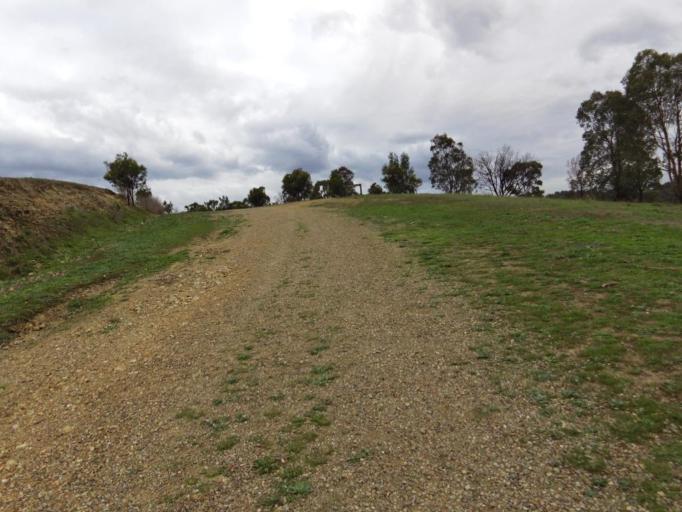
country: AU
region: Victoria
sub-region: Yarra Ranges
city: Chirnside Park
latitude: -37.7142
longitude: 145.2895
